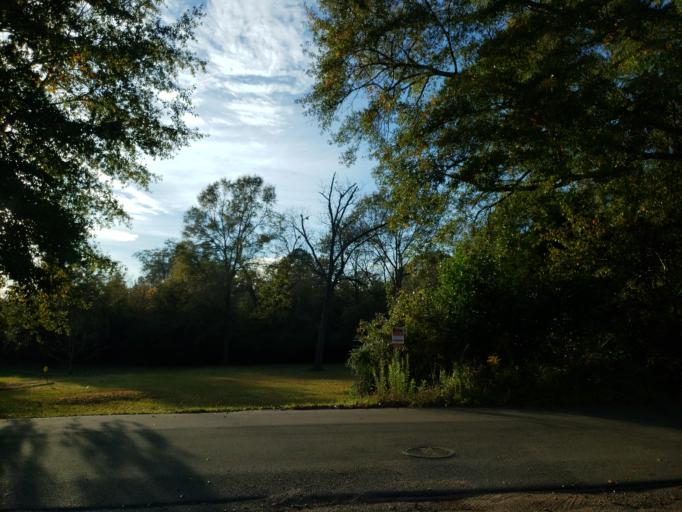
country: US
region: Mississippi
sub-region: Lamar County
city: Purvis
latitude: 31.1442
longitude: -89.4138
